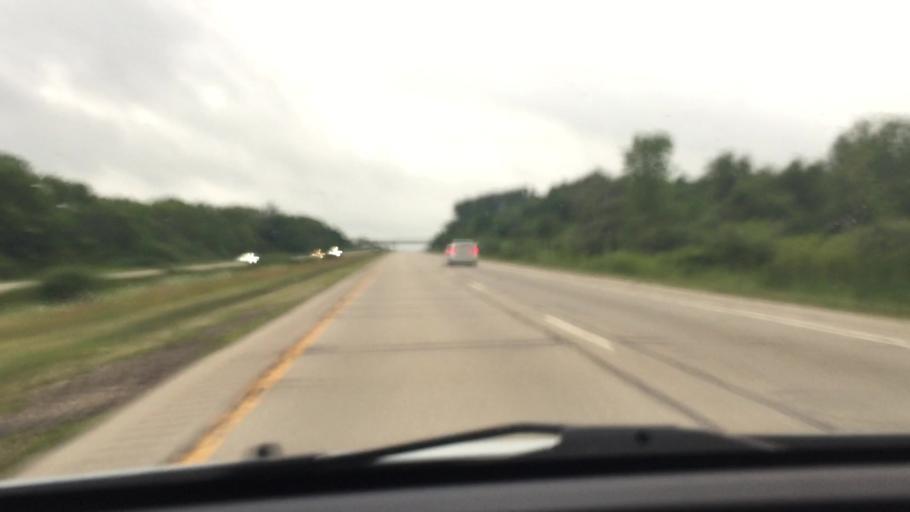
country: US
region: Wisconsin
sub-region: Walworth County
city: Como
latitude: 42.6250
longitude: -88.4660
